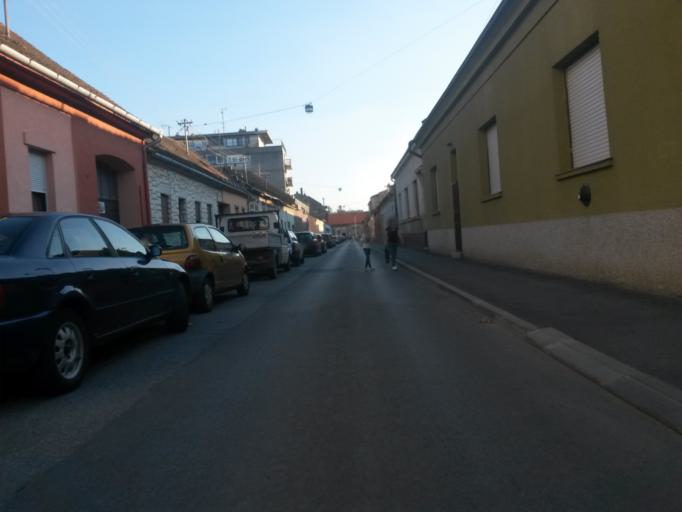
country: HR
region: Osjecko-Baranjska
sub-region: Grad Osijek
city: Osijek
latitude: 45.5595
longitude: 18.6739
